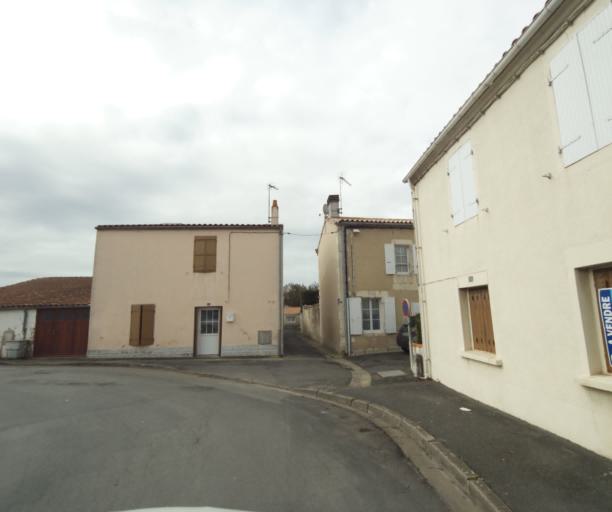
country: FR
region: Poitou-Charentes
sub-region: Departement de la Charente-Maritime
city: Lagord
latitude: 46.1898
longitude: -1.1525
